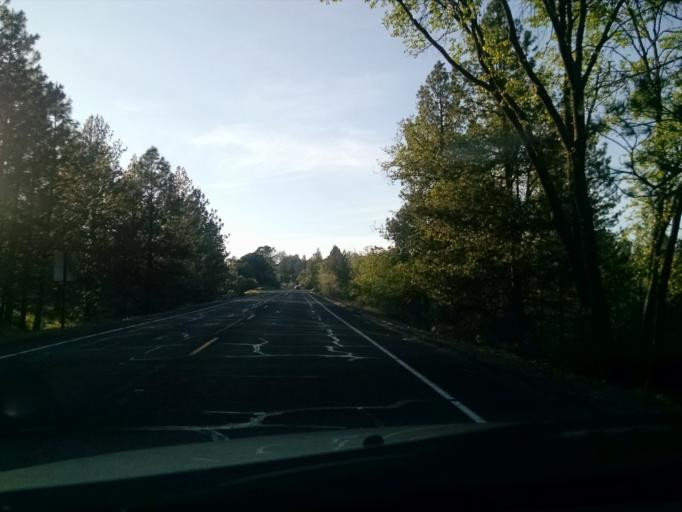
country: US
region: California
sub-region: Madera County
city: Ahwahnee
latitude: 37.4515
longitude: -119.7628
